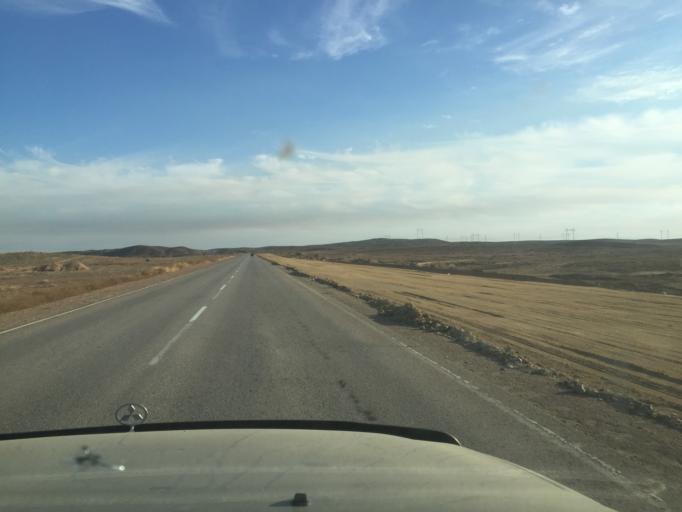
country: KZ
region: Zhambyl
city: Mynaral
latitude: 45.5196
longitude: 73.4895
